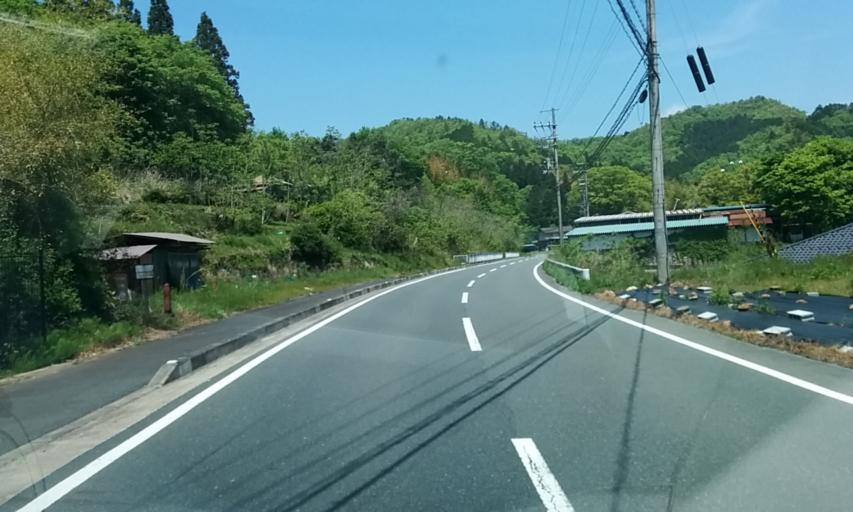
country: JP
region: Kyoto
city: Ayabe
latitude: 35.2468
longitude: 135.2659
